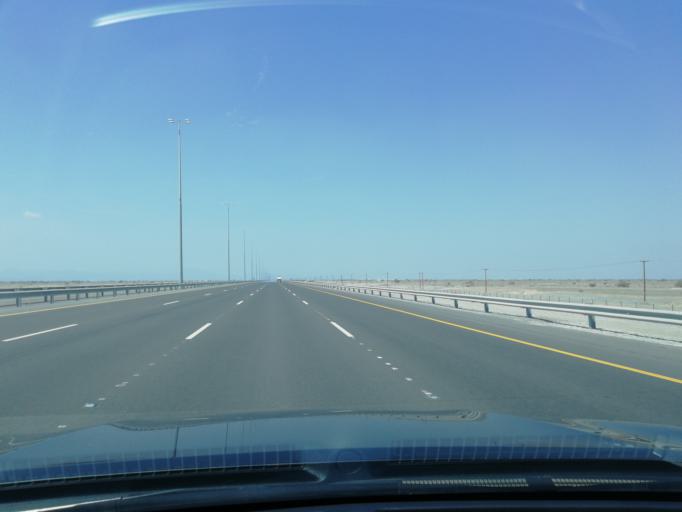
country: OM
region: Al Batinah
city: Barka'
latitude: 23.6017
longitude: 57.8184
